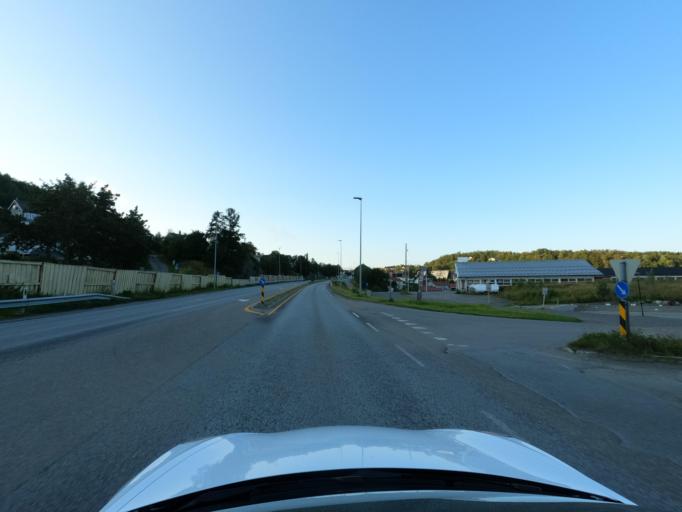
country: NO
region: Troms
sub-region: Harstad
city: Harstad
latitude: 68.7731
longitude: 16.5593
